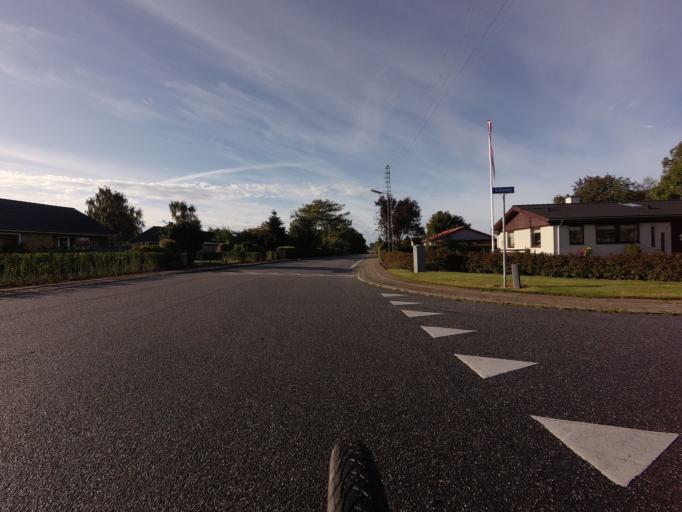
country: DK
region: Central Jutland
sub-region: Viborg Kommune
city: Bjerringbro
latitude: 56.4804
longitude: 9.6246
